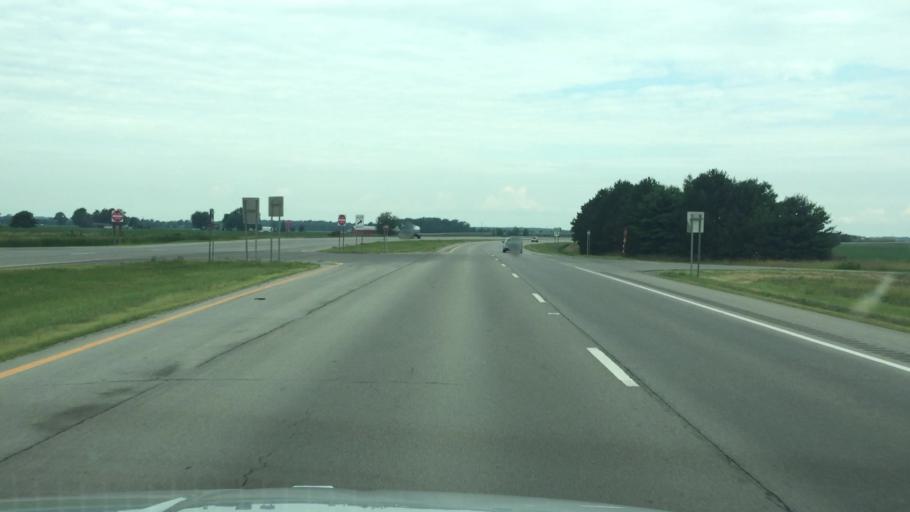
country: US
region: Ohio
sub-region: Wyandot County
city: Carey
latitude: 40.9653
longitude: -83.4762
